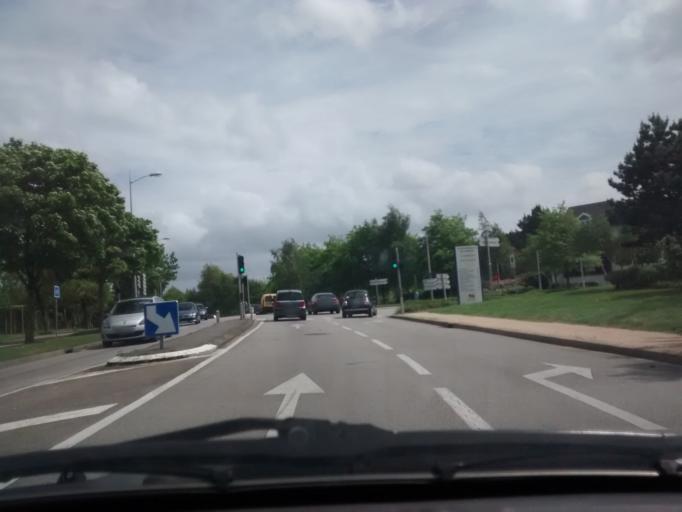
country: FR
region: Brittany
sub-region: Departement du Morbihan
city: Vannes
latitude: 47.6424
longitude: -2.7761
